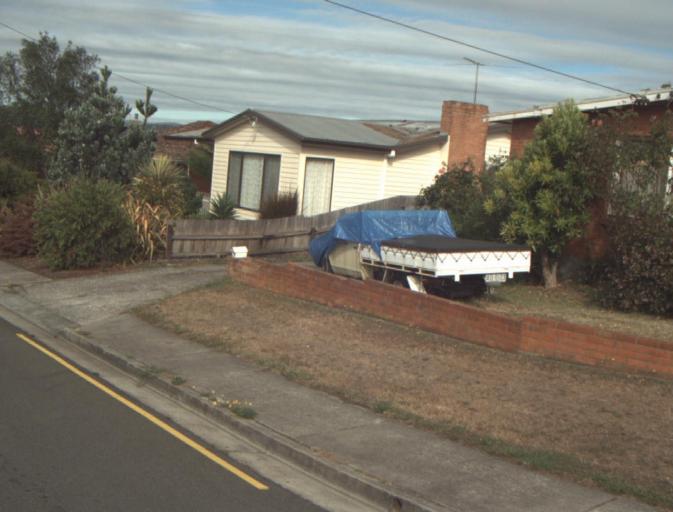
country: AU
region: Tasmania
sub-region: Launceston
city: Invermay
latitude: -41.3905
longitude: 147.1352
